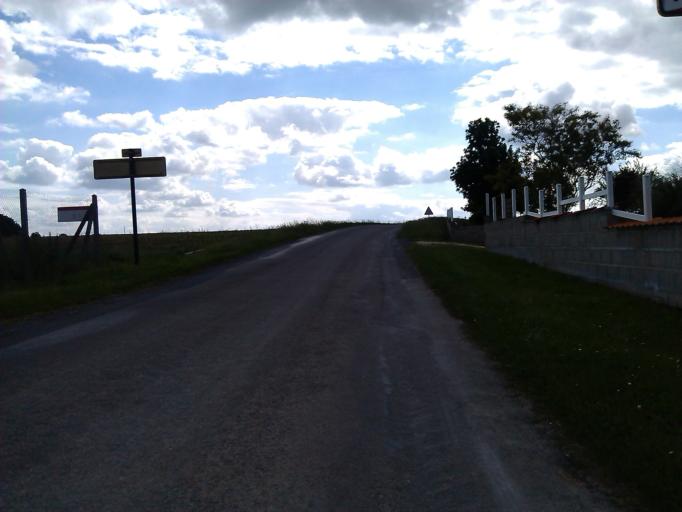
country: FR
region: Poitou-Charentes
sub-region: Departement de la Charente
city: Mansle
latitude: 45.8931
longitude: 0.1955
